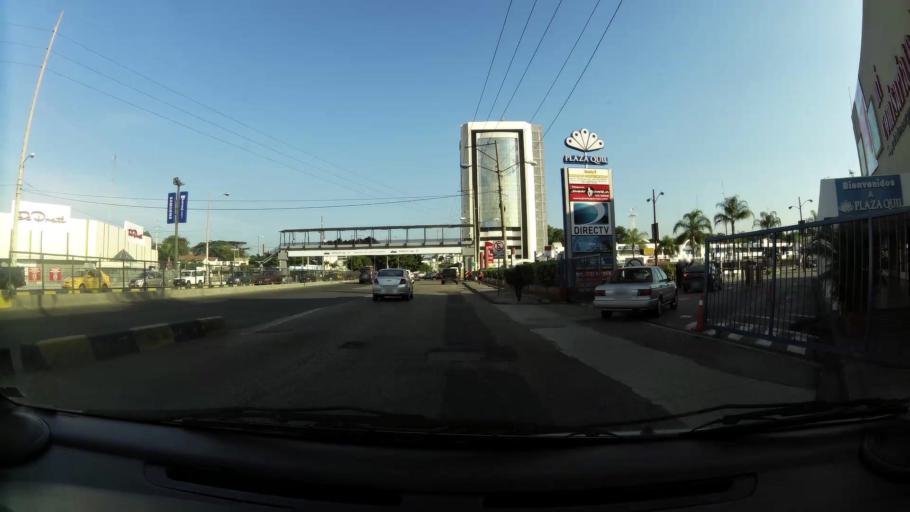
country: EC
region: Guayas
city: Guayaquil
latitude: -2.1696
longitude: -79.8995
